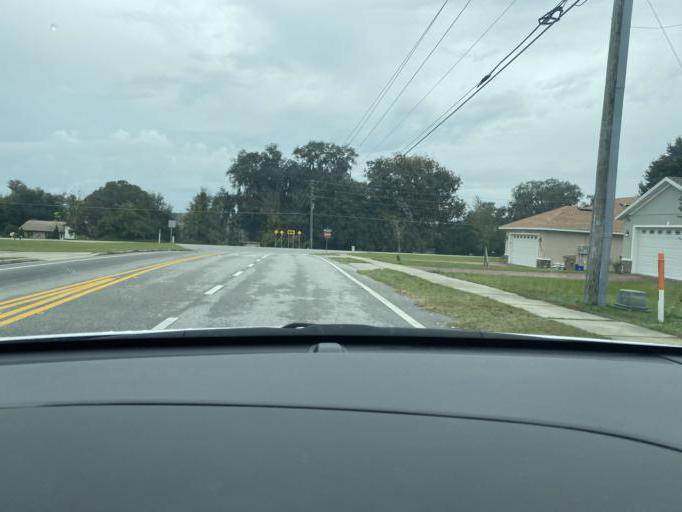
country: US
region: Florida
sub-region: Lake County
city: Mascotte
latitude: 28.5769
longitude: -81.8673
